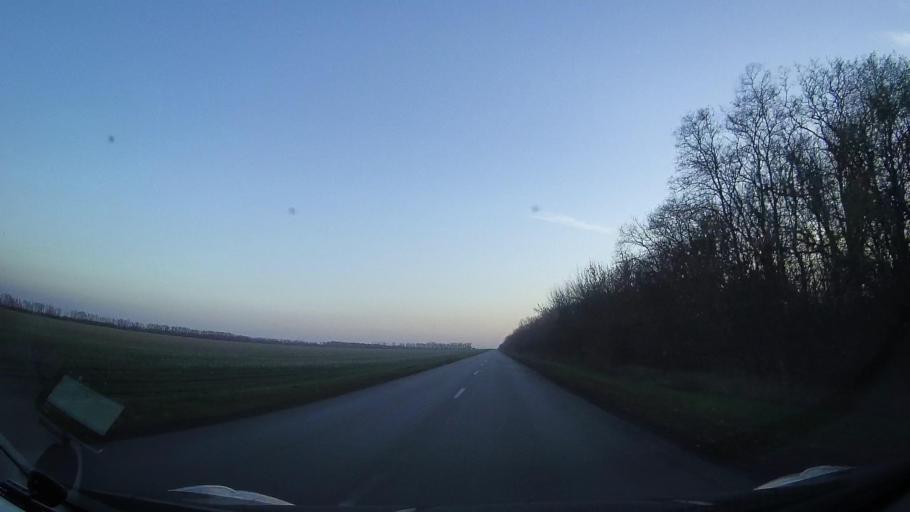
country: RU
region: Rostov
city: Zernograd
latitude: 47.0387
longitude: 40.3915
